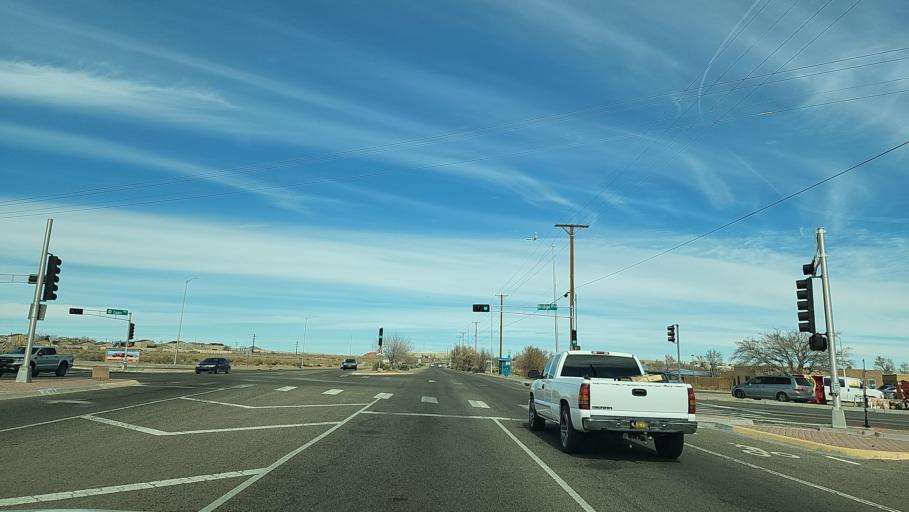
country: US
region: New Mexico
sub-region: Bernalillo County
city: Albuquerque
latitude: 35.0697
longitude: -106.7117
